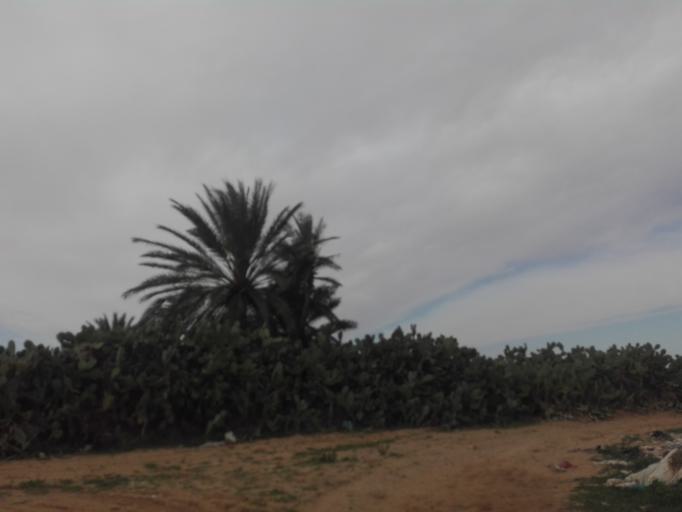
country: TN
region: Safaqis
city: Sfax
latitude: 34.7390
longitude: 10.5018
